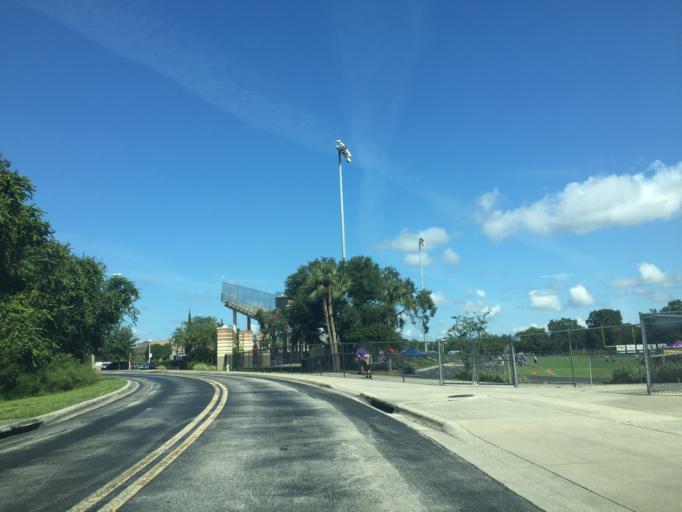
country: US
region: Florida
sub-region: Seminole County
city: Winter Springs
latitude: 28.7016
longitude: -81.2619
